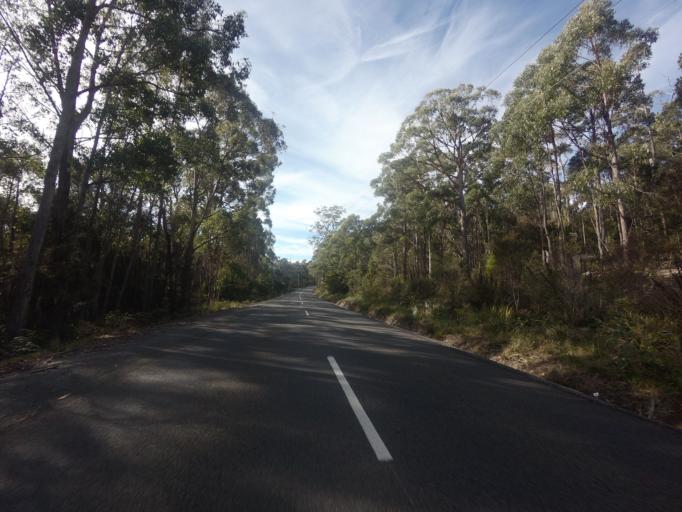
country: AU
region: Tasmania
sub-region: Clarence
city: Sandford
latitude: -43.0608
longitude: 147.8438
